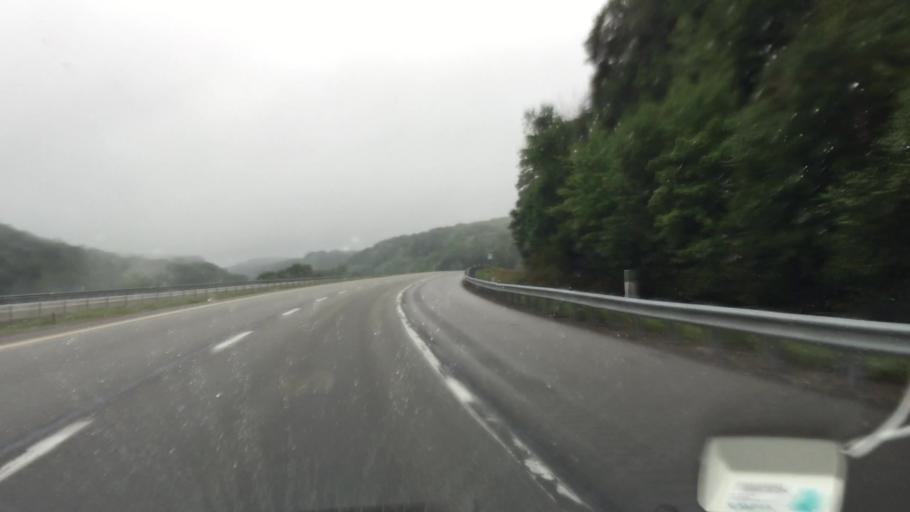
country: US
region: Pennsylvania
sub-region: Allegheny County
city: Franklin Park
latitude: 40.5658
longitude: -80.0895
